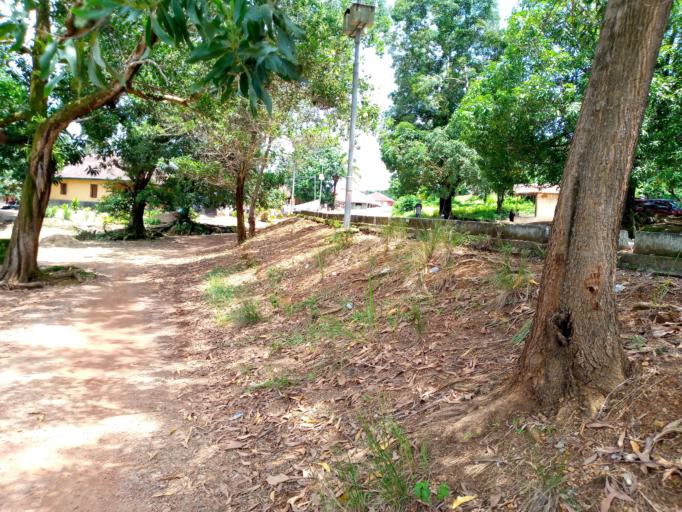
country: SL
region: Northern Province
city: Magburaka
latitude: 8.7280
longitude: -11.9462
